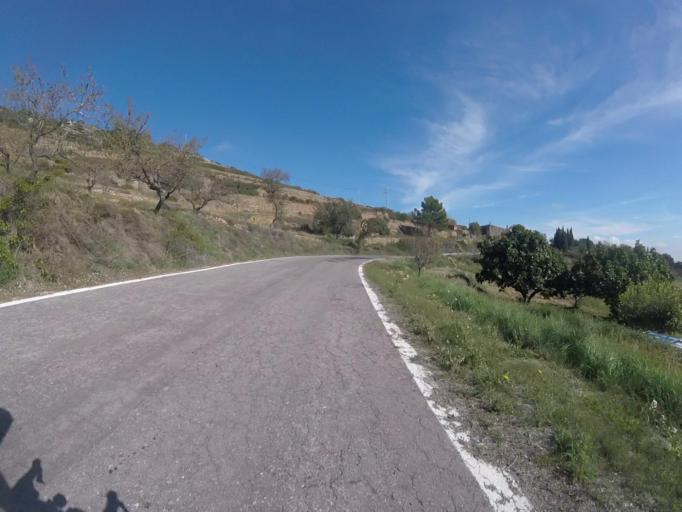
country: ES
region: Valencia
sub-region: Provincia de Castello
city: Sarratella
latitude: 40.3205
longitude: 0.0287
